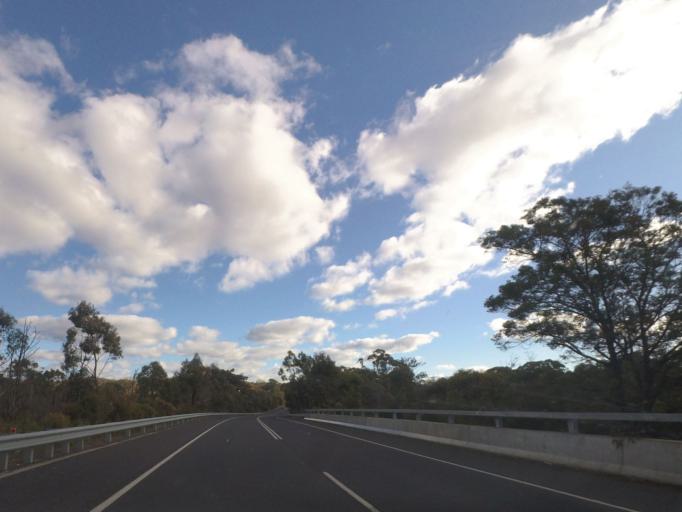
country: AU
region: Victoria
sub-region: Mount Alexander
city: Castlemaine
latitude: -37.1023
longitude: 144.3190
